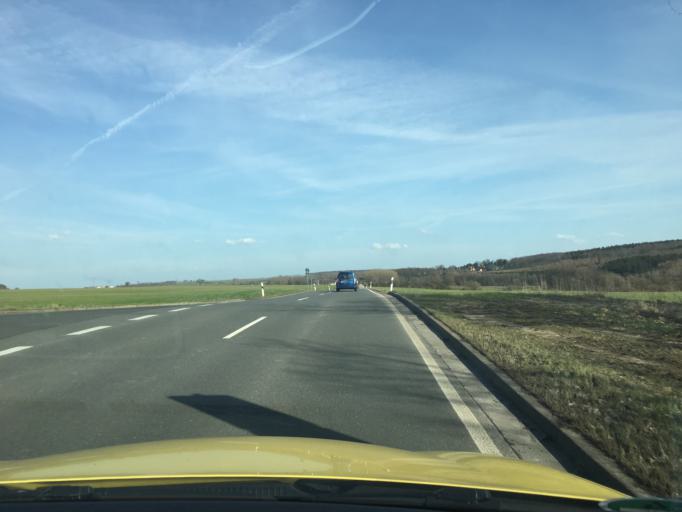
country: DE
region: Thuringia
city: Rastenberg
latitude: 51.2037
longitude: 11.4291
